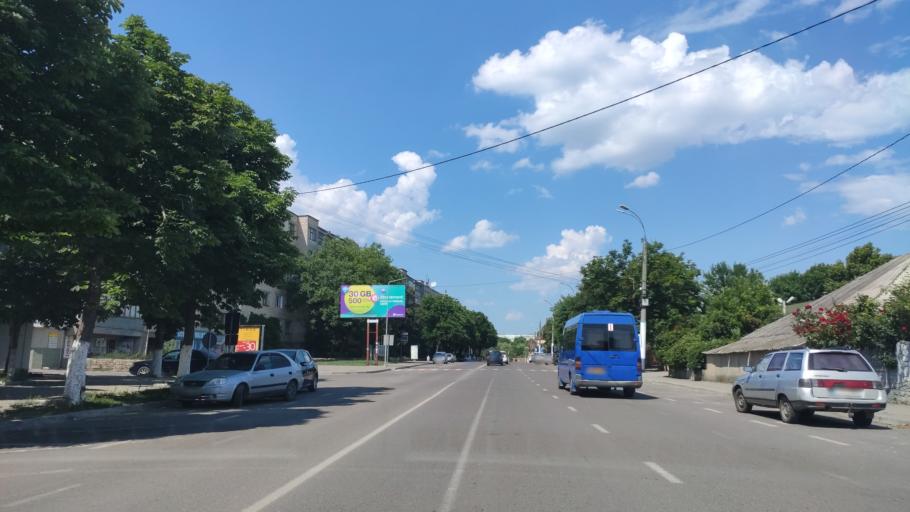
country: MD
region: Raionul Soroca
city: Soroca
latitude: 48.1598
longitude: 28.3030
